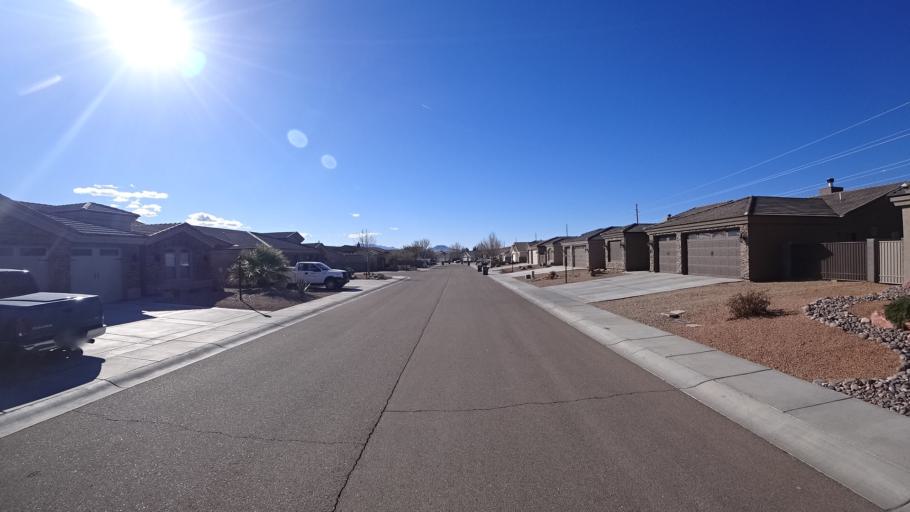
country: US
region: Arizona
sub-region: Mohave County
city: New Kingman-Butler
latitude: 35.2381
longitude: -114.0331
